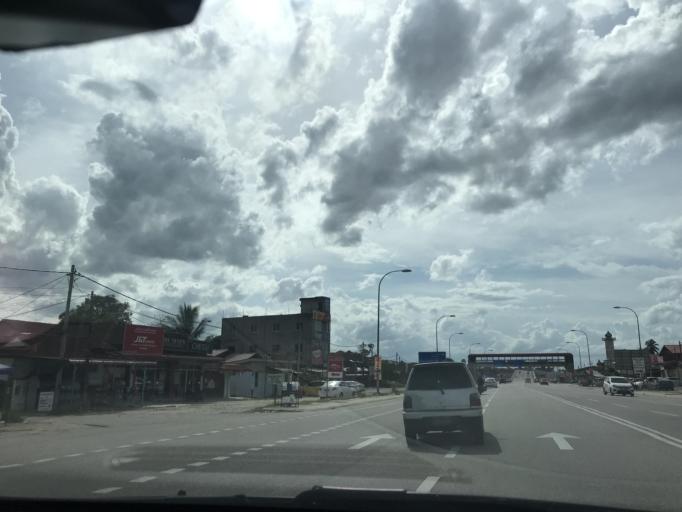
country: MY
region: Kelantan
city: Kampung Lemal
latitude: 6.0255
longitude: 102.1462
